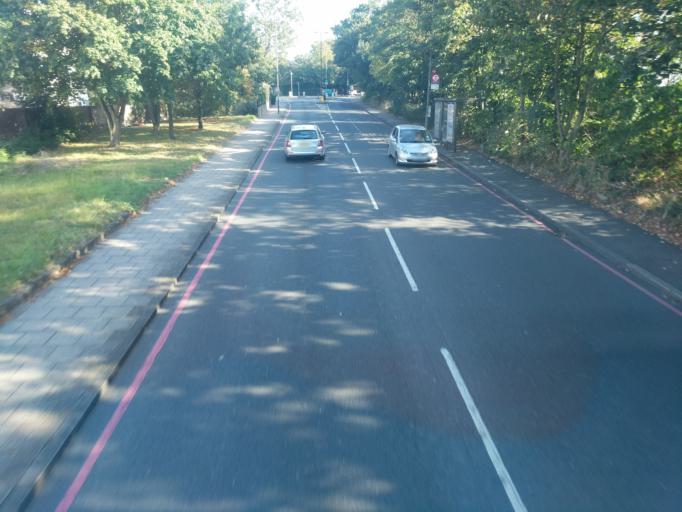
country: GB
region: England
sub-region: Greater London
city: Bromley
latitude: 51.4166
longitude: 0.0049
